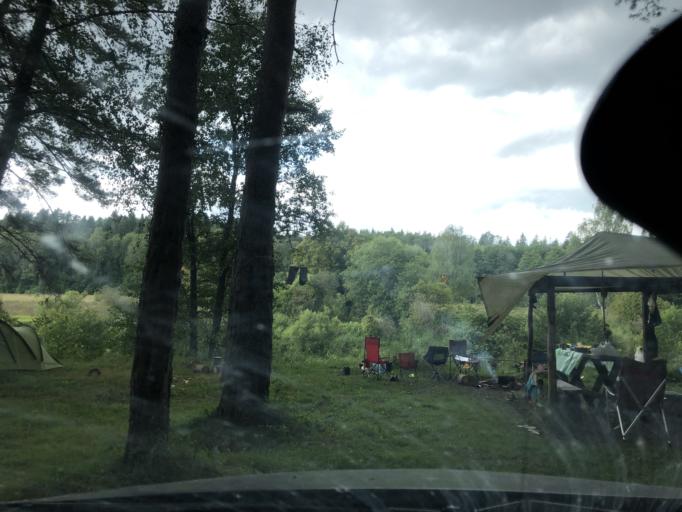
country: RU
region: Kaluga
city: Yukhnov
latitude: 54.7272
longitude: 35.1150
